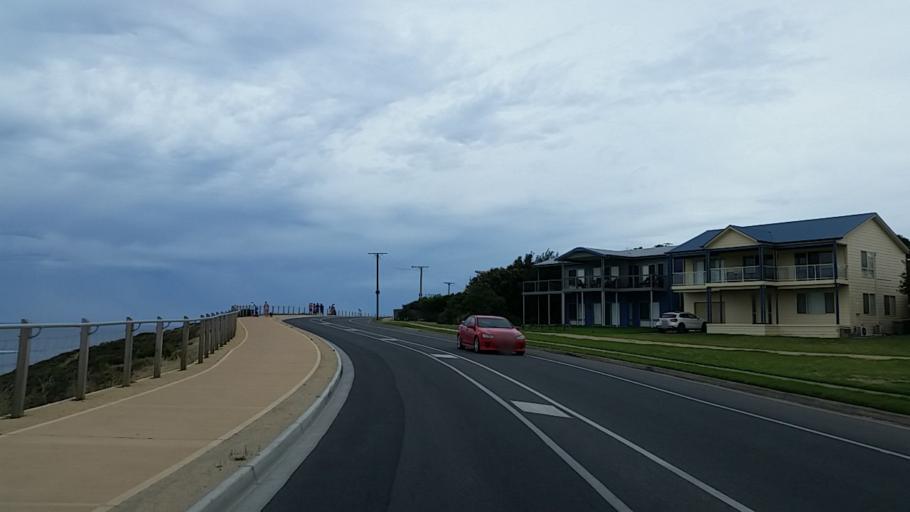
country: AU
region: South Australia
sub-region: Onkaparinga
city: Port Willunga
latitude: -35.2864
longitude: 138.4447
